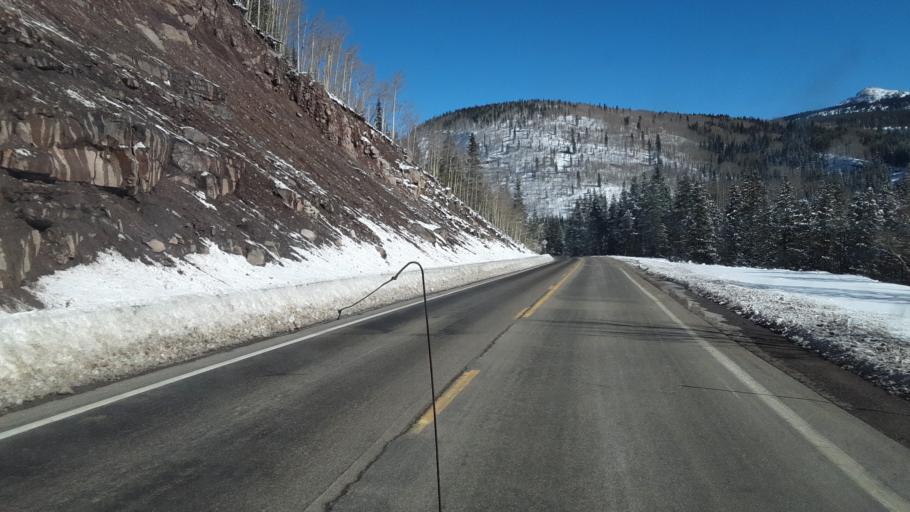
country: US
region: Colorado
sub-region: San Juan County
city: Silverton
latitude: 37.7191
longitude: -107.7561
